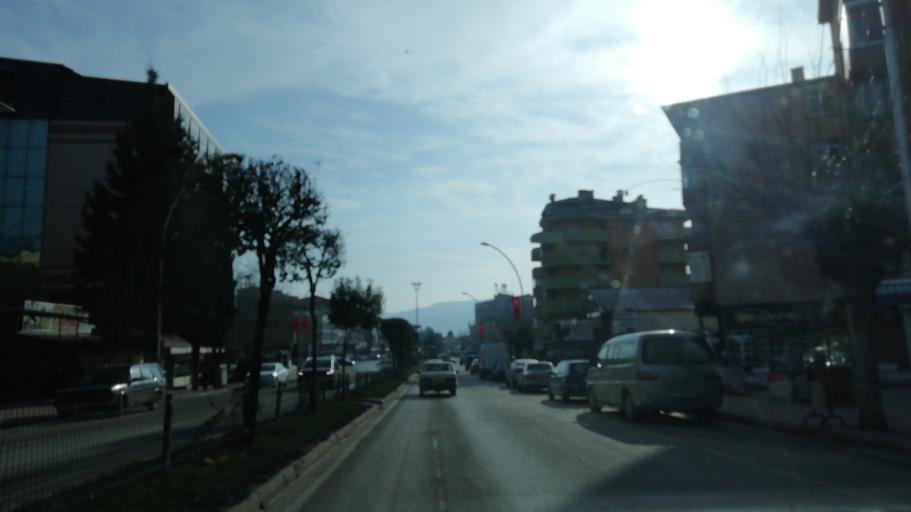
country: TR
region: Karabuk
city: Safranbolu
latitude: 41.2518
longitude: 32.6804
